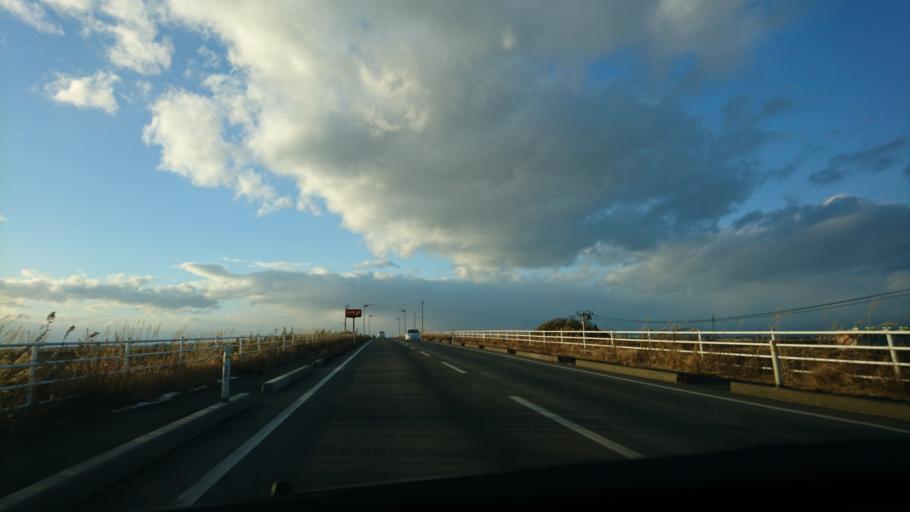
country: JP
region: Miyagi
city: Wakuya
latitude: 38.7204
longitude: 141.1565
